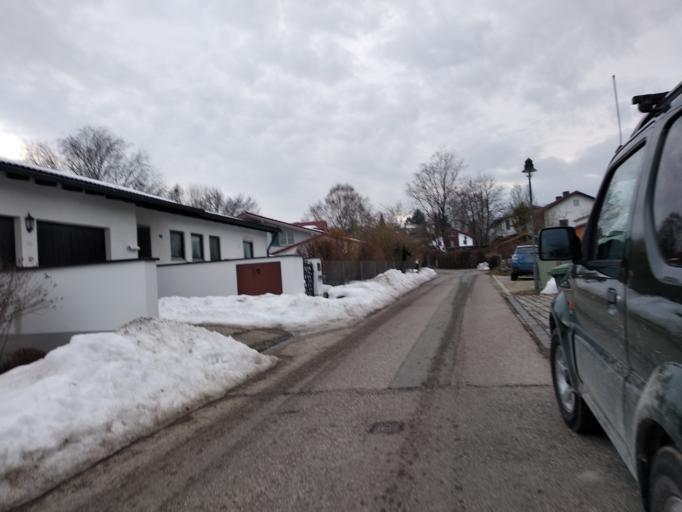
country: DE
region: Bavaria
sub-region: Upper Bavaria
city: Ebersberg
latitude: 48.0825
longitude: 11.9788
